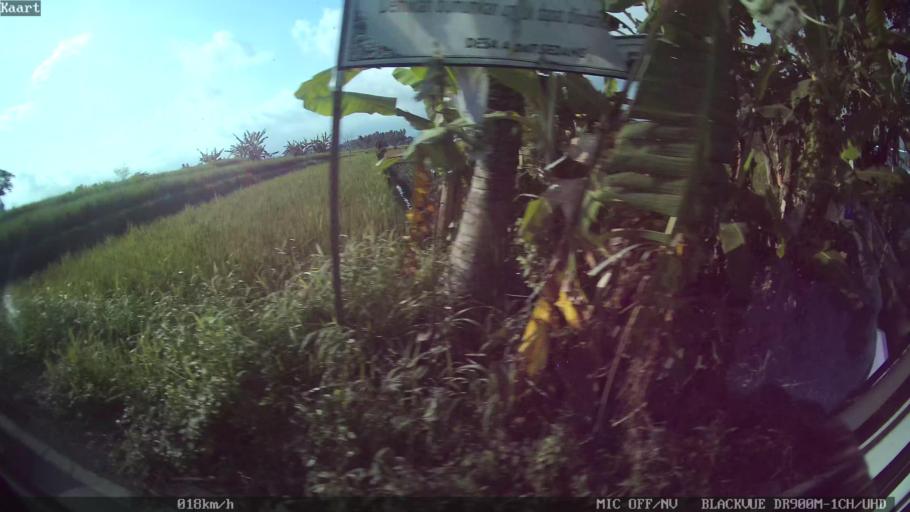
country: ID
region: Bali
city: Banjar Desa
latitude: -8.5797
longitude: 115.2343
